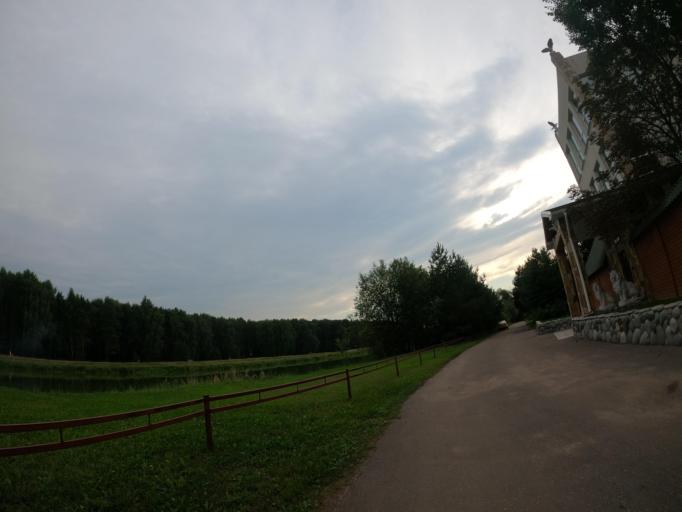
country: RU
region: Moskovskaya
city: Bykovo
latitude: 55.6524
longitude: 38.1091
